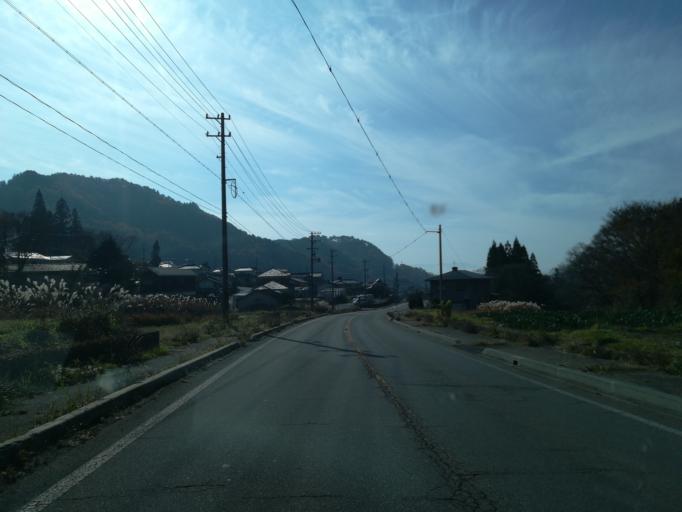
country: JP
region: Nagano
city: Ueda
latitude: 36.4524
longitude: 138.3308
